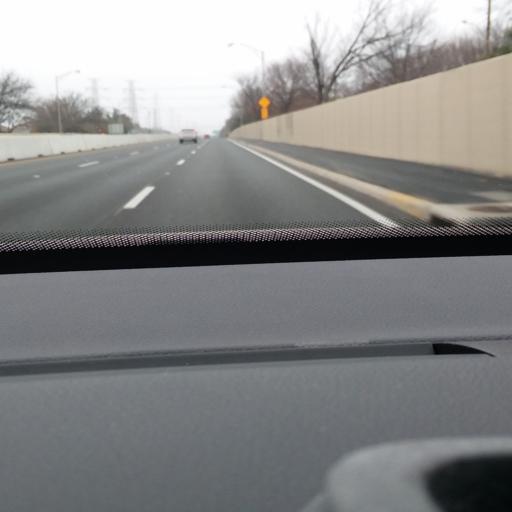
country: US
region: Texas
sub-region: Dallas County
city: University Park
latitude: 32.8794
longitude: -96.8013
